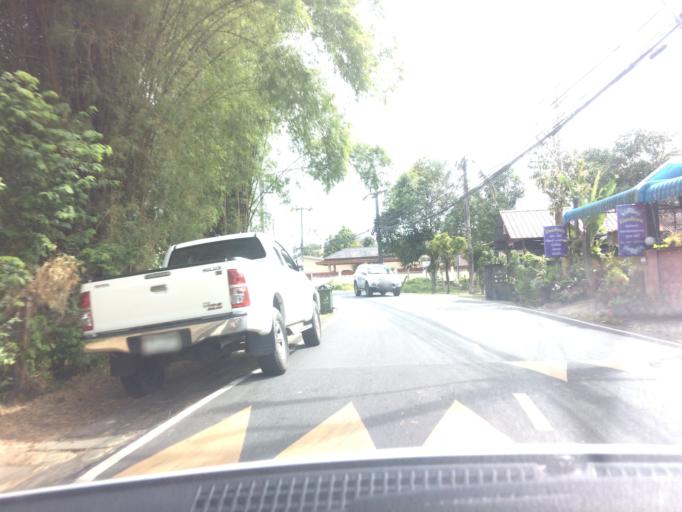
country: TH
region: Phuket
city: Thalang
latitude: 8.0310
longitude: 98.3414
